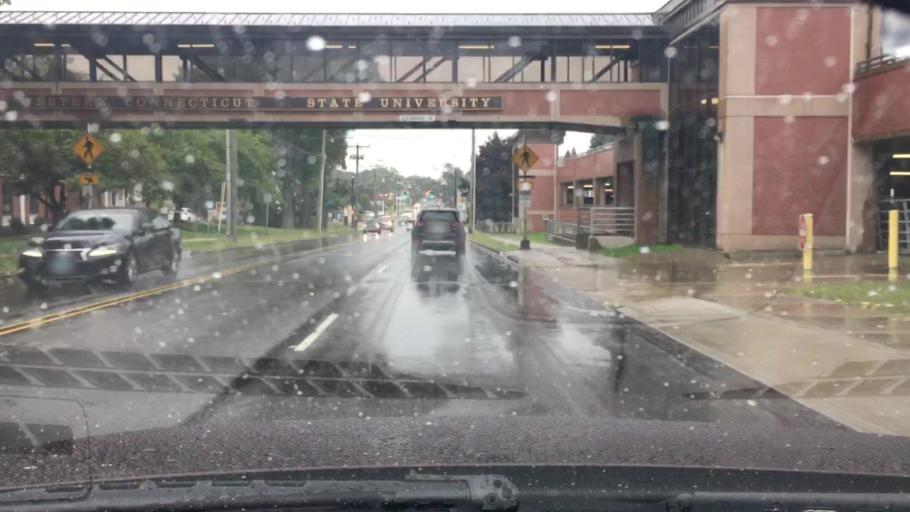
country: US
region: Connecticut
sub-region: Fairfield County
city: Danbury
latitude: 41.3994
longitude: -73.4437
